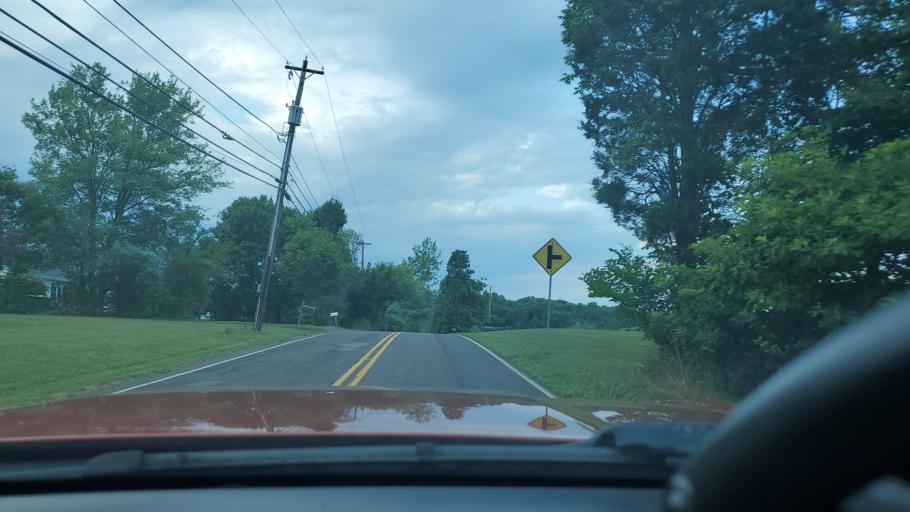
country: US
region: Pennsylvania
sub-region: Montgomery County
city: Limerick
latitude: 40.2569
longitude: -75.5221
